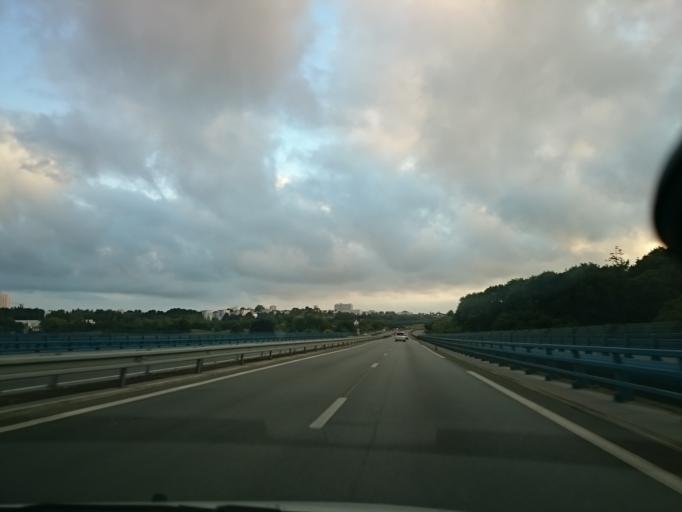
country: FR
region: Brittany
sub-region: Departement du Morbihan
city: Lorient
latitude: 47.7743
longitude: -3.3685
